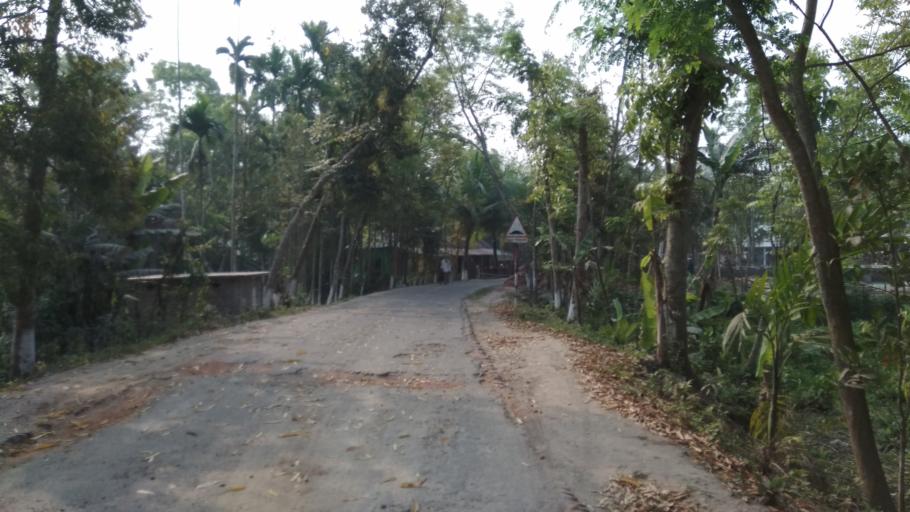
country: BD
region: Barisal
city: Mehendiganj
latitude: 22.9545
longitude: 90.4153
